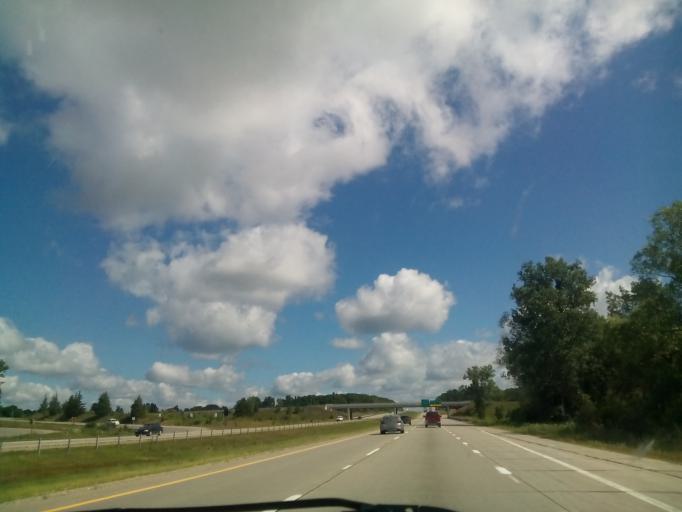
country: US
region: Michigan
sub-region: Genesee County
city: Linden
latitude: 42.7663
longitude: -83.7537
